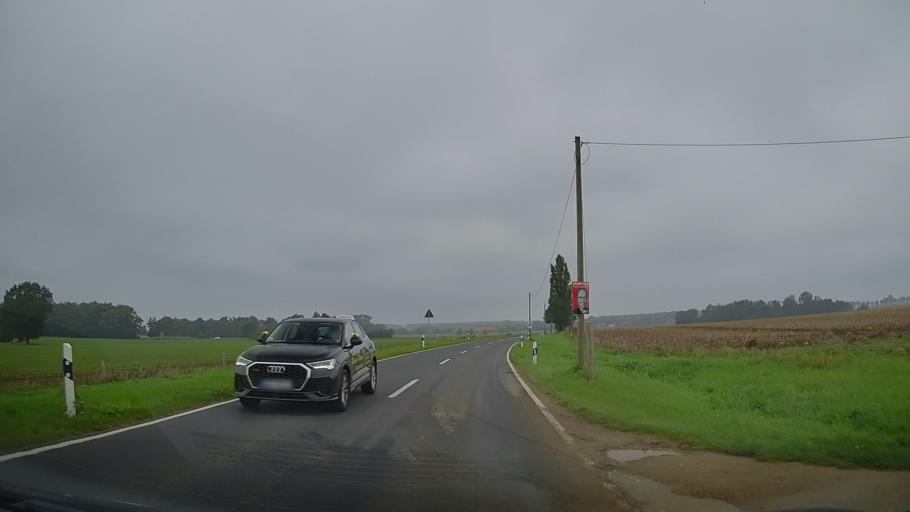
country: DE
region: Mecklenburg-Vorpommern
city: Neubukow
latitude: 54.0647
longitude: 11.6268
